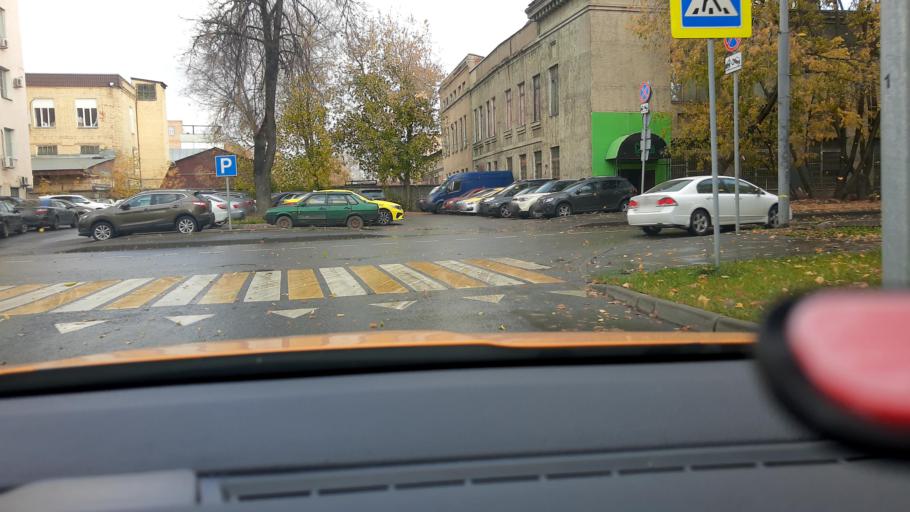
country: RU
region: Moscow
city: Lefortovo
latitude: 55.7766
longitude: 37.7317
